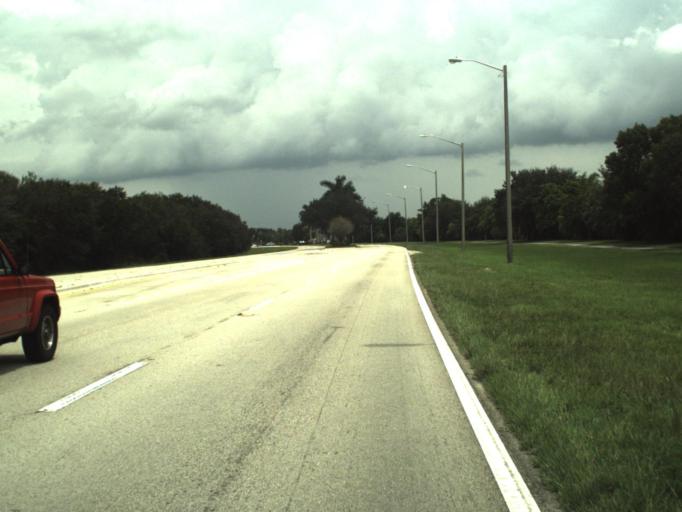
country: US
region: Florida
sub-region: Broward County
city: Sunshine Ranches
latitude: 26.0289
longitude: -80.3210
